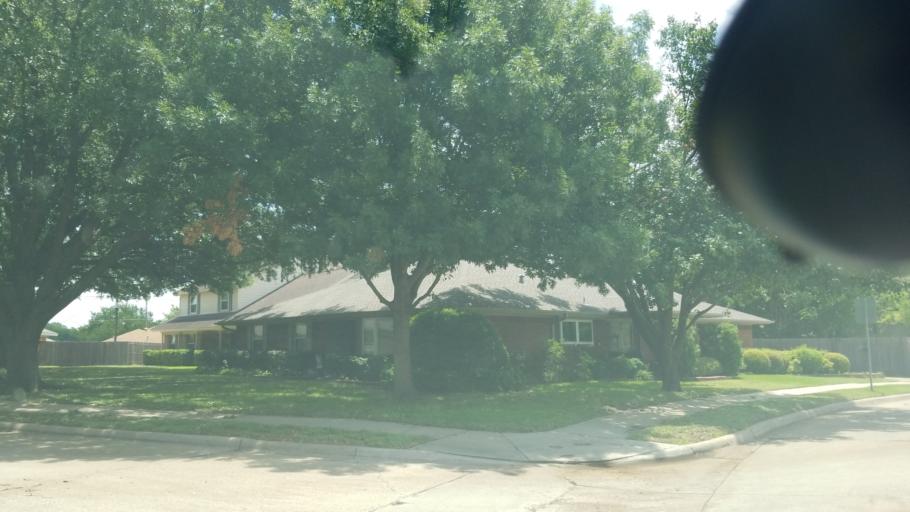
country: US
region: Texas
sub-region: Dallas County
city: Irving
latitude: 32.8470
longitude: -96.9666
